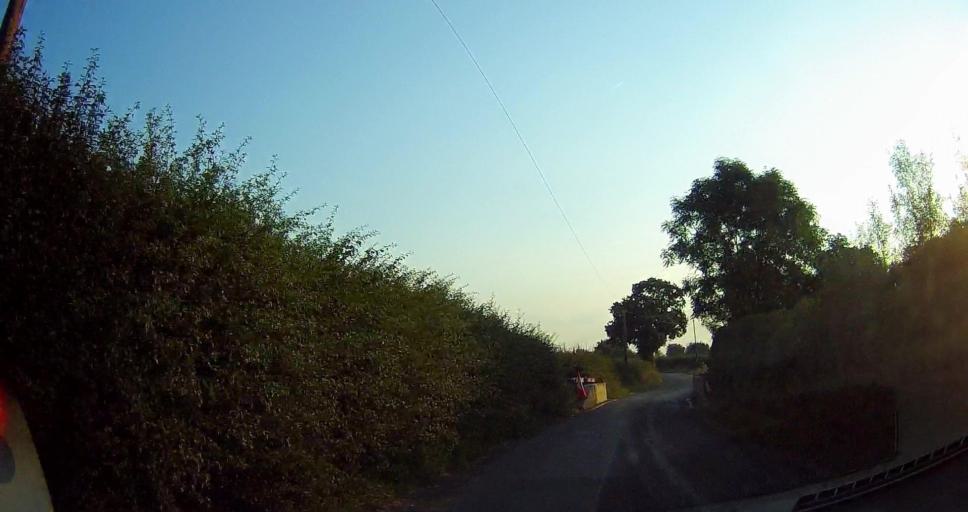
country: GB
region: England
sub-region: Cheshire East
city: Nantwich
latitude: 53.0073
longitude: -2.5278
